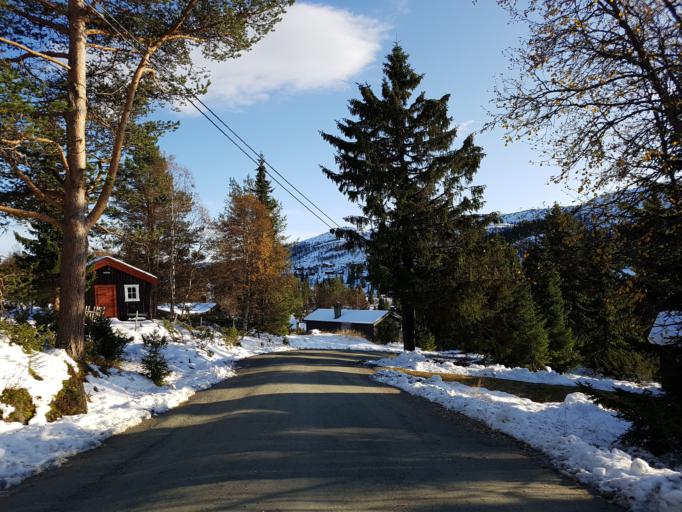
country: NO
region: Oppland
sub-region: Sel
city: Otta
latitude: 61.8099
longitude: 9.6880
